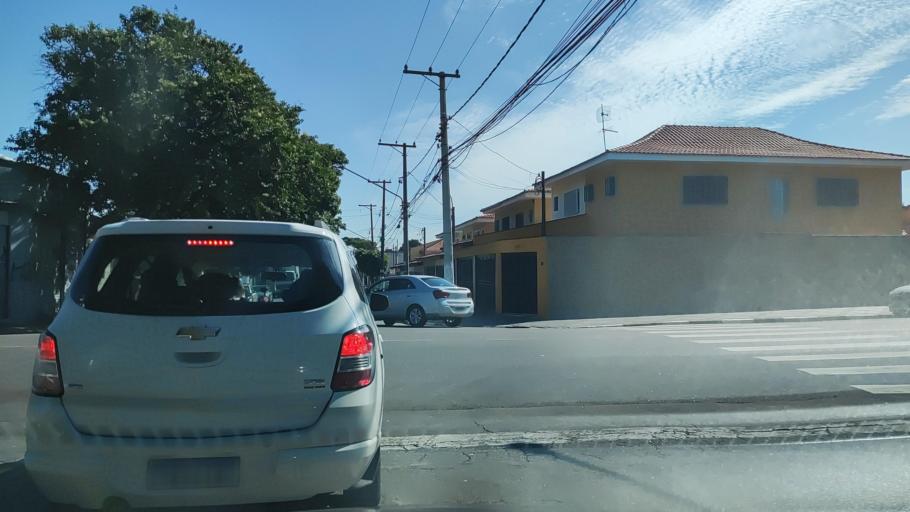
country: BR
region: Sao Paulo
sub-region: Osasco
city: Osasco
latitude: -23.5292
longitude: -46.7662
